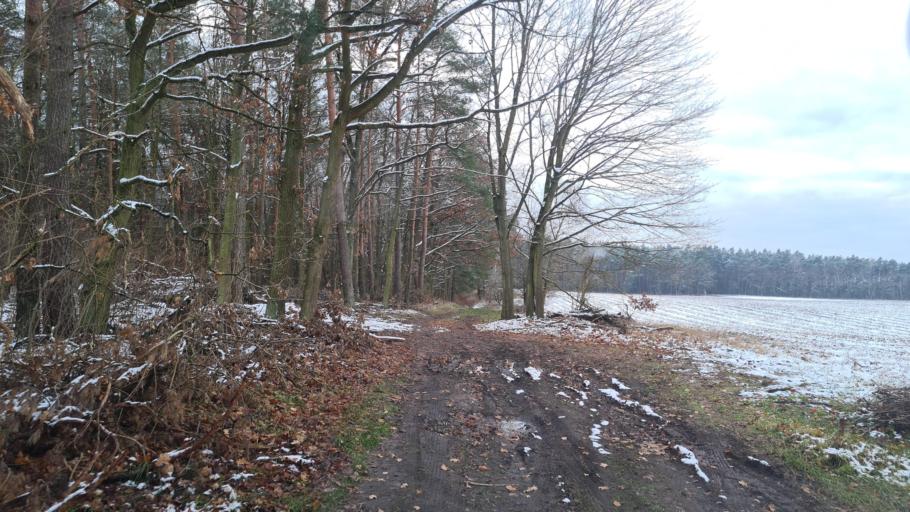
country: DE
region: Brandenburg
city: Strausberg
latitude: 52.5584
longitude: 13.9084
